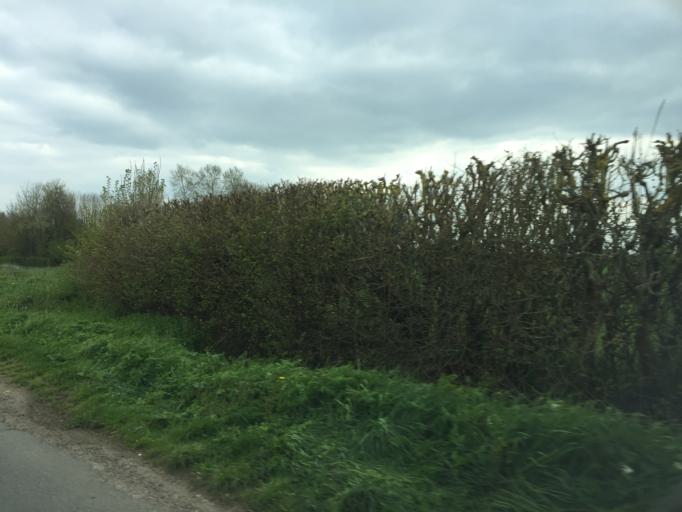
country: GB
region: England
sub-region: Oxfordshire
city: Bicester
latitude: 51.9372
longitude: -1.1258
